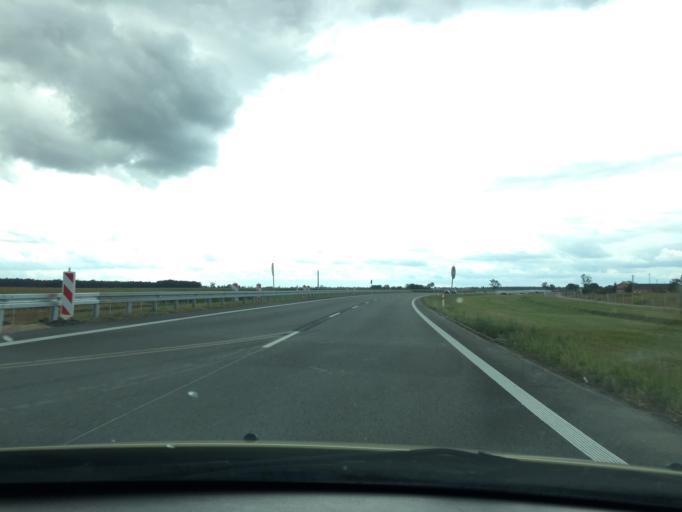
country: PL
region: Greater Poland Voivodeship
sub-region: Powiat sredzki
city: Nowe Miasto nad Warta
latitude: 52.0460
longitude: 17.4452
